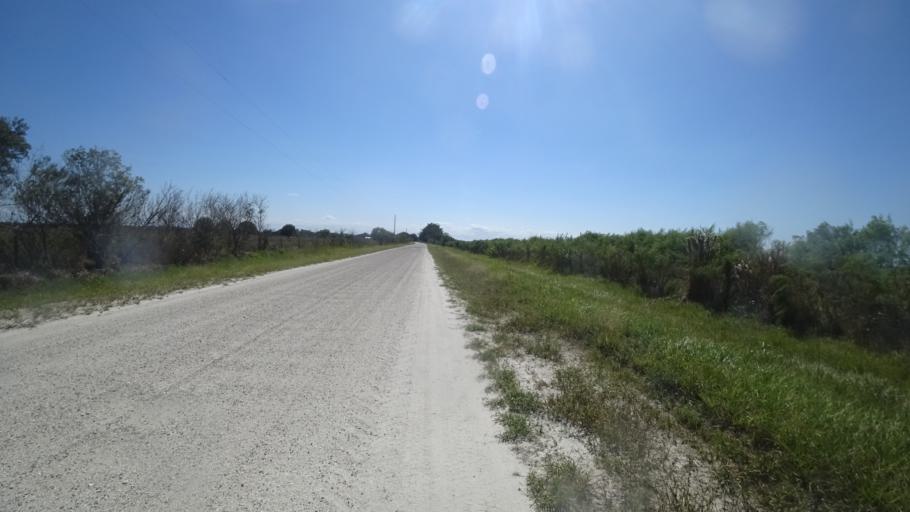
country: US
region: Florida
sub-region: DeSoto County
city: Arcadia
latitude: 27.3299
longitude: -82.0806
